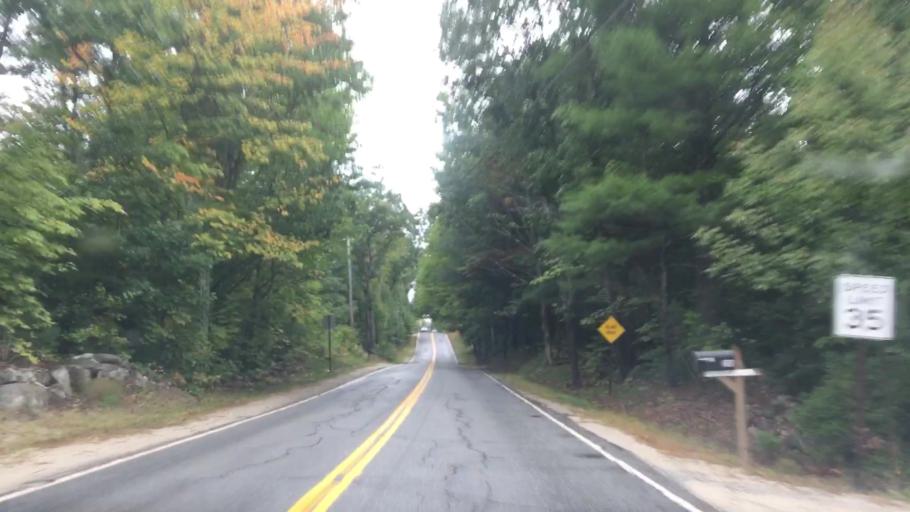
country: US
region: Maine
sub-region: Cumberland County
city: Raymond
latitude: 43.9751
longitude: -70.4697
